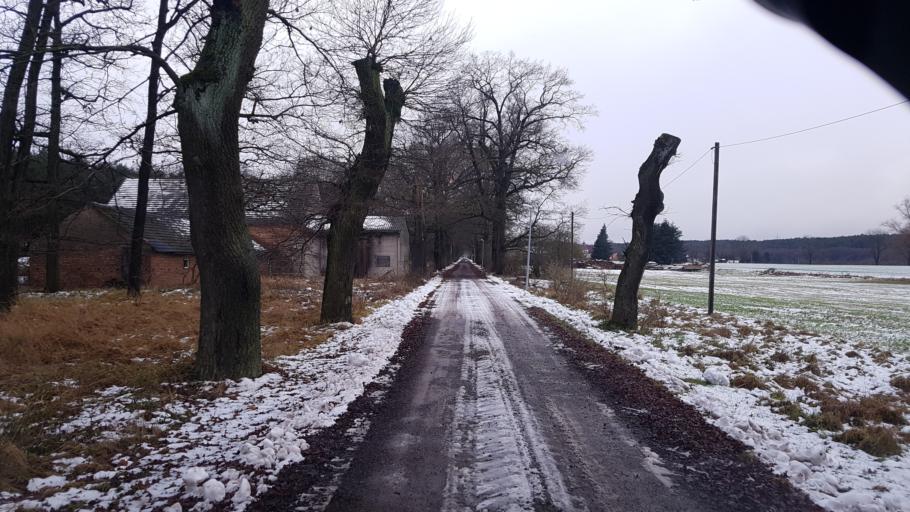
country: DE
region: Brandenburg
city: Schenkendobern
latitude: 51.9666
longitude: 14.5821
